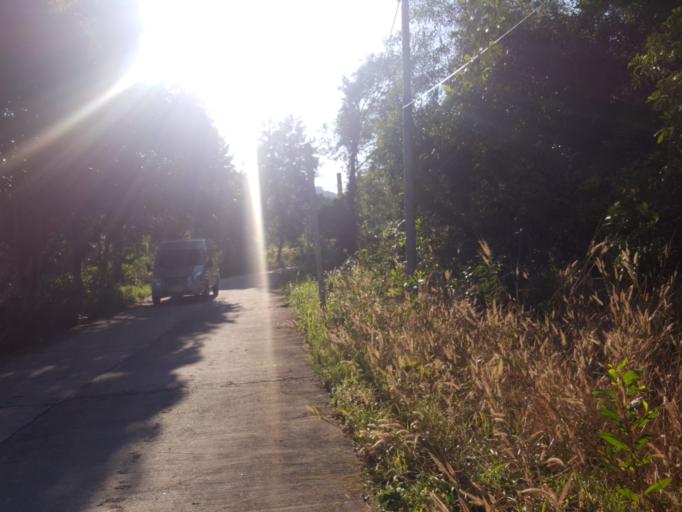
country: VN
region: Kien Giang
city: Duong GJong
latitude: 10.0596
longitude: 104.0344
